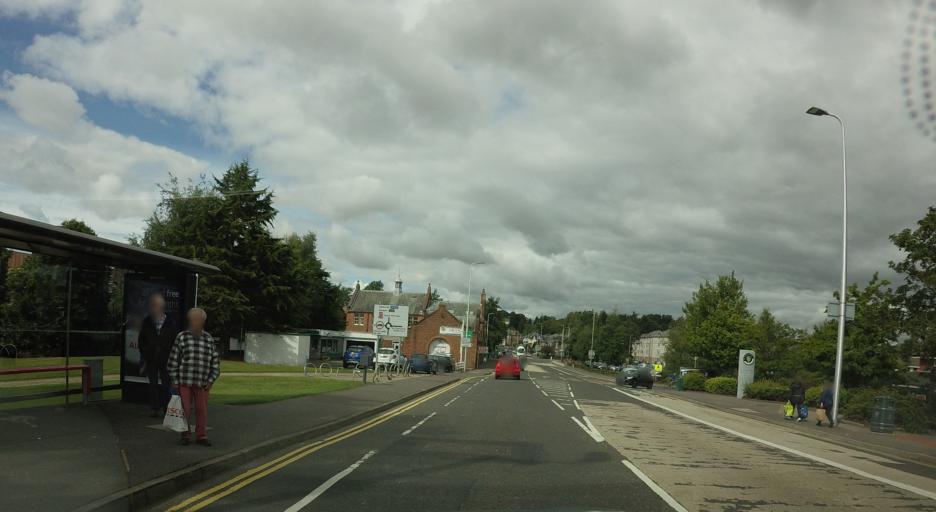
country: GB
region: Scotland
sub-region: Perth and Kinross
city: Perth
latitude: 56.3956
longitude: -3.4430
